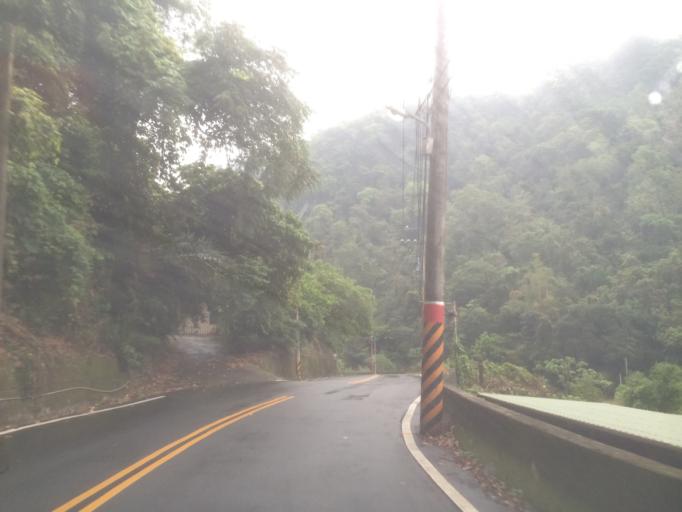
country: TW
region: Taiwan
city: Fengyuan
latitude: 24.1676
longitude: 120.8279
